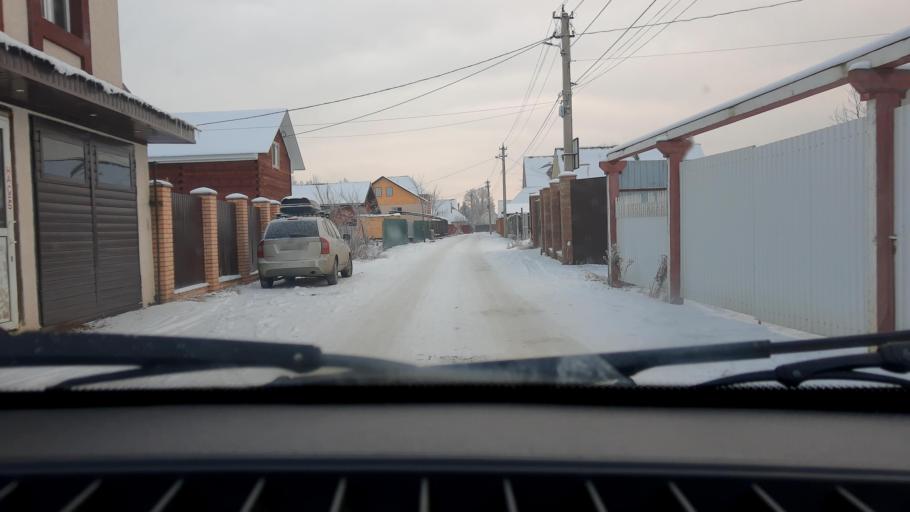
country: RU
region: Bashkortostan
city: Ufa
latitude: 54.6588
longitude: 55.9250
